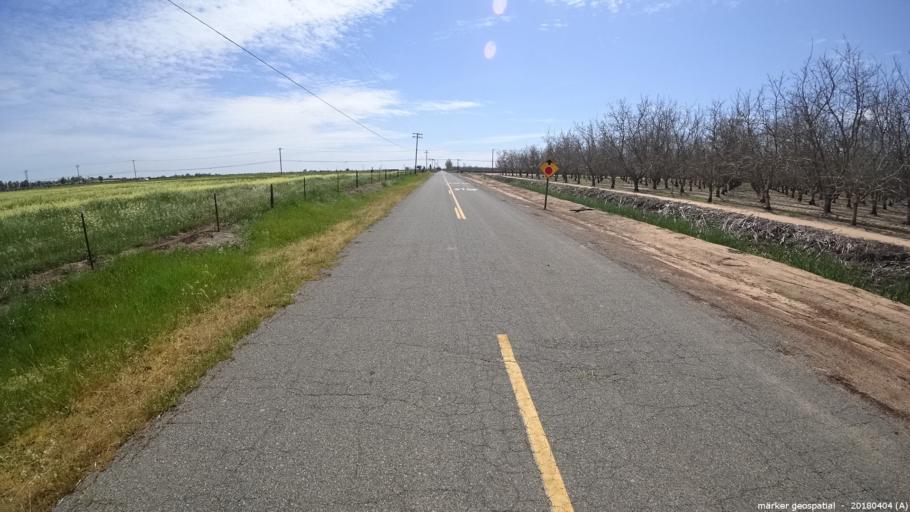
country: US
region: California
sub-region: Sacramento County
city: Herald
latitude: 38.2939
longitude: -121.2081
